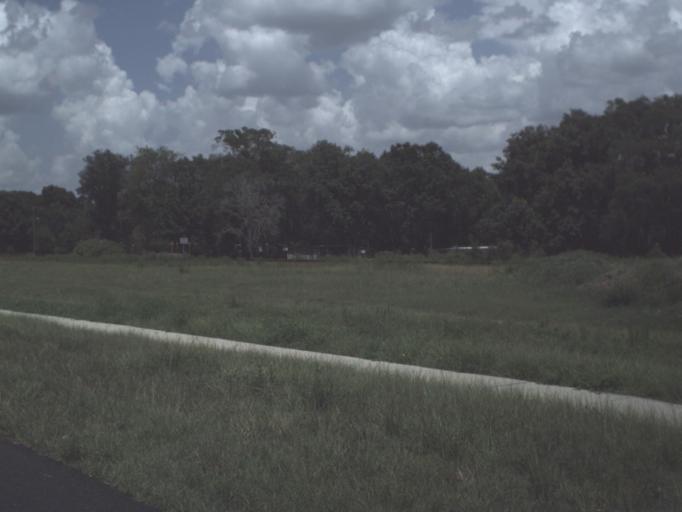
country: US
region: Florida
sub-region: Pasco County
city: Lacoochee
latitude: 28.4448
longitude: -82.1887
